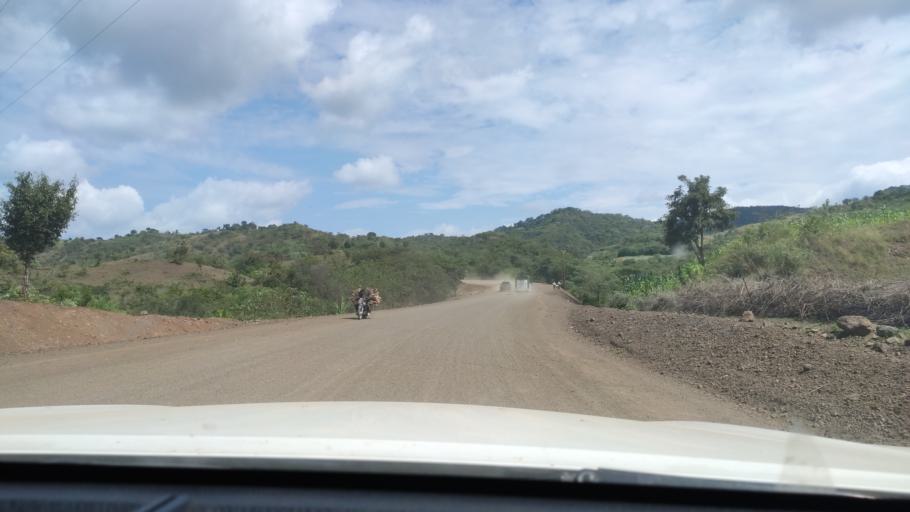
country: ET
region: Southern Nations, Nationalities, and People's Region
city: Felege Neway
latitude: 6.3912
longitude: 37.0610
